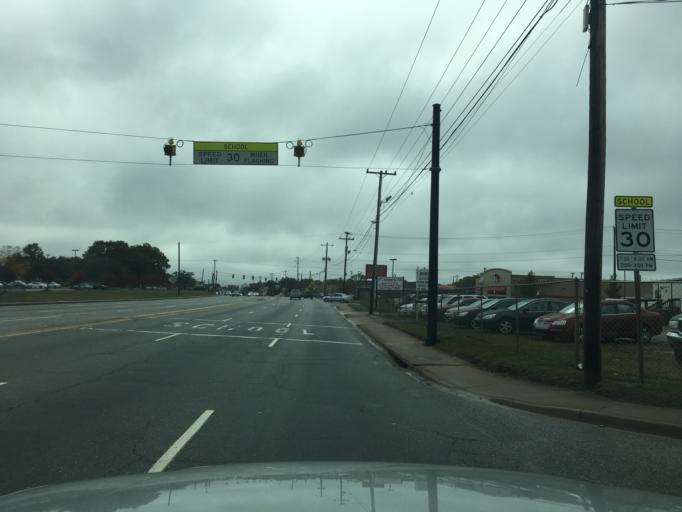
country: US
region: South Carolina
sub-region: Greenville County
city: Welcome
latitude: 34.8217
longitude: -82.4459
